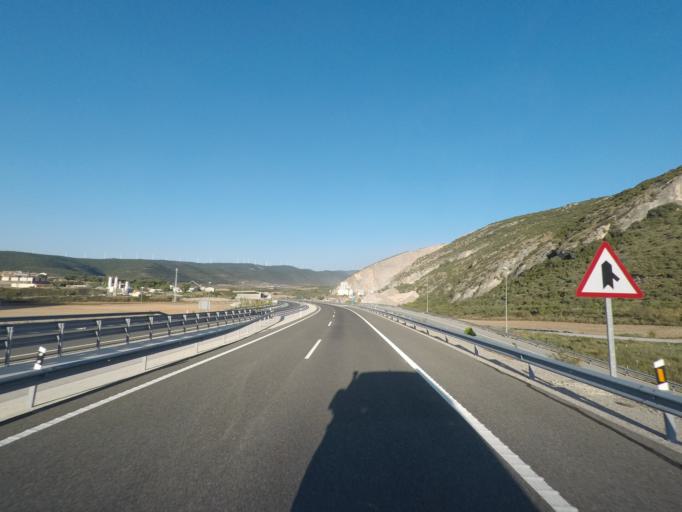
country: ES
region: Navarre
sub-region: Provincia de Navarra
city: Liedena
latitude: 42.6237
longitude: -1.2721
